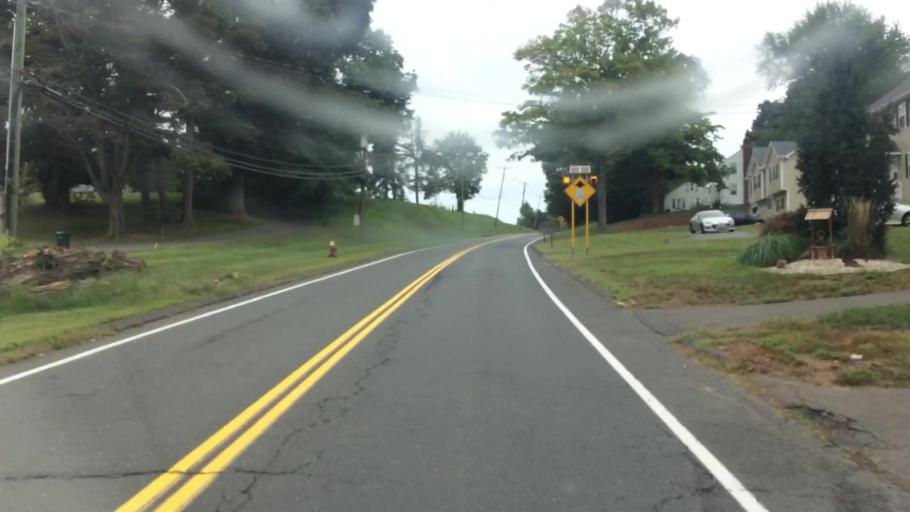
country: US
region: Connecticut
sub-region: Hartford County
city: Glastonbury Center
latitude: 41.6591
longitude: -72.6367
